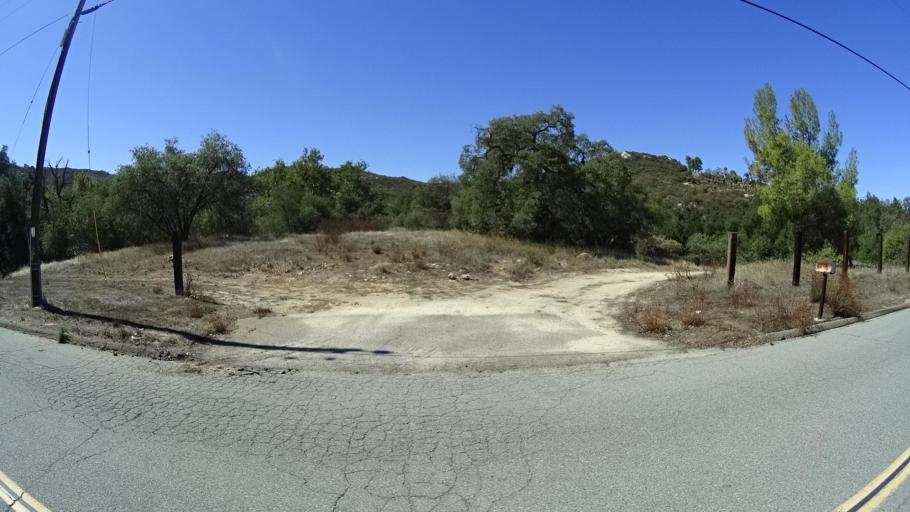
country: US
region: California
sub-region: San Diego County
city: Alpine
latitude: 32.7447
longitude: -116.7548
